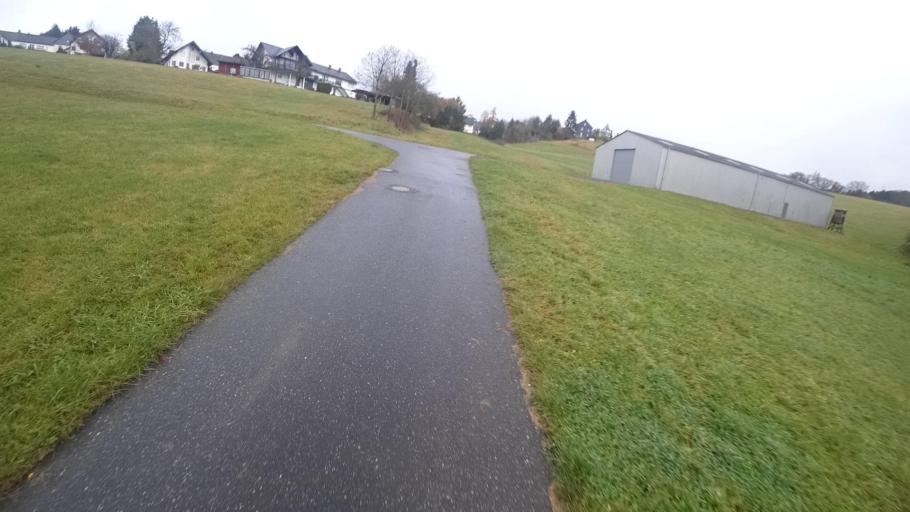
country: DE
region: Rheinland-Pfalz
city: Emmelshausen
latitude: 50.1422
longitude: 7.5740
